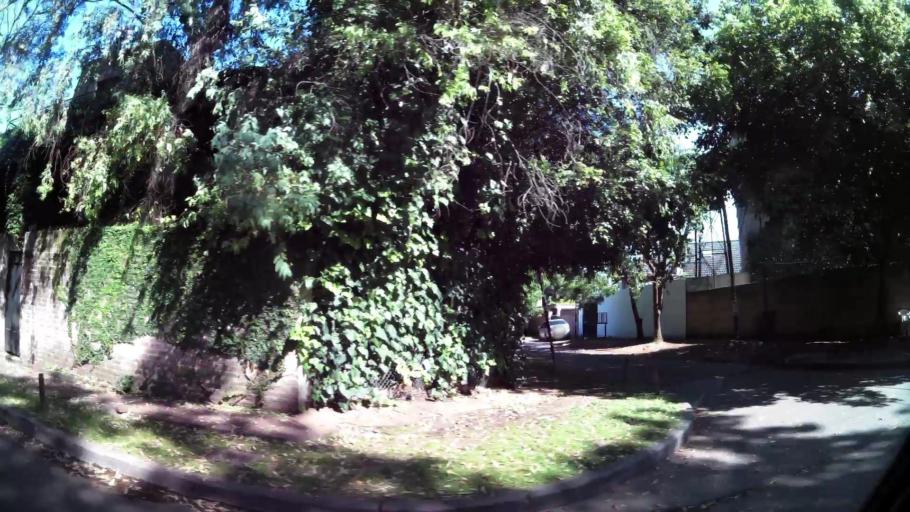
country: AR
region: Buenos Aires
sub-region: Partido de Tigre
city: Tigre
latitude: -34.4858
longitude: -58.5776
